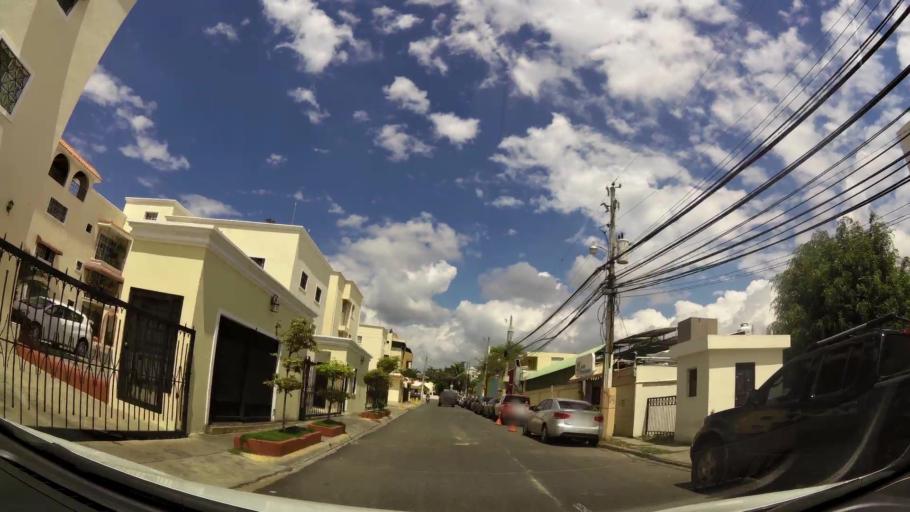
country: DO
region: Santiago
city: Santiago de los Caballeros
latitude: 19.4587
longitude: -70.6621
